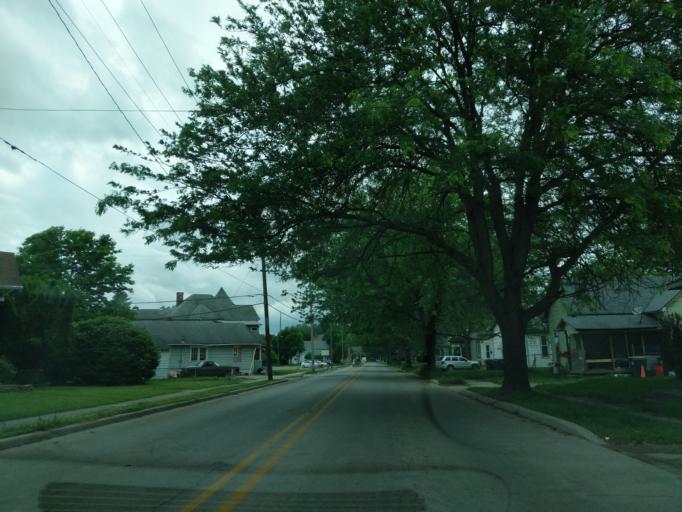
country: US
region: Indiana
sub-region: Madison County
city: Anderson
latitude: 40.1009
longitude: -85.6706
